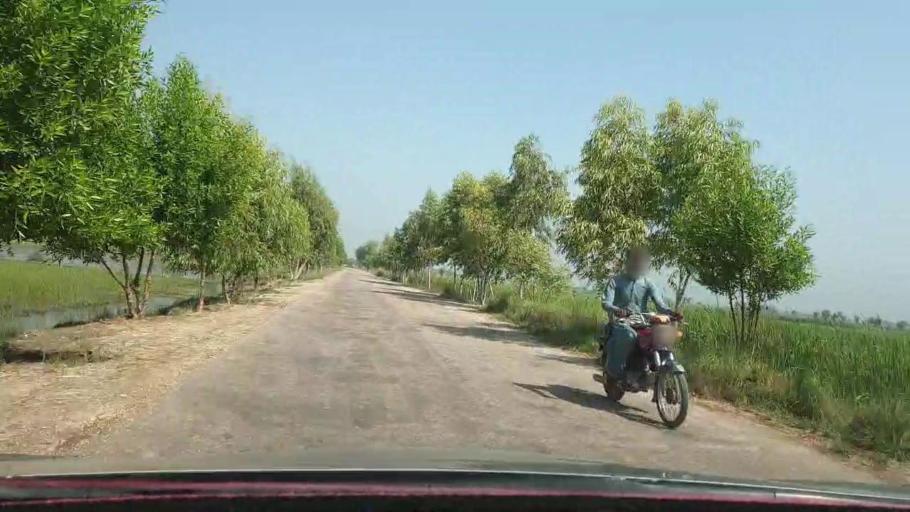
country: PK
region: Sindh
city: Warah
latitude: 27.4682
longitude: 67.8336
